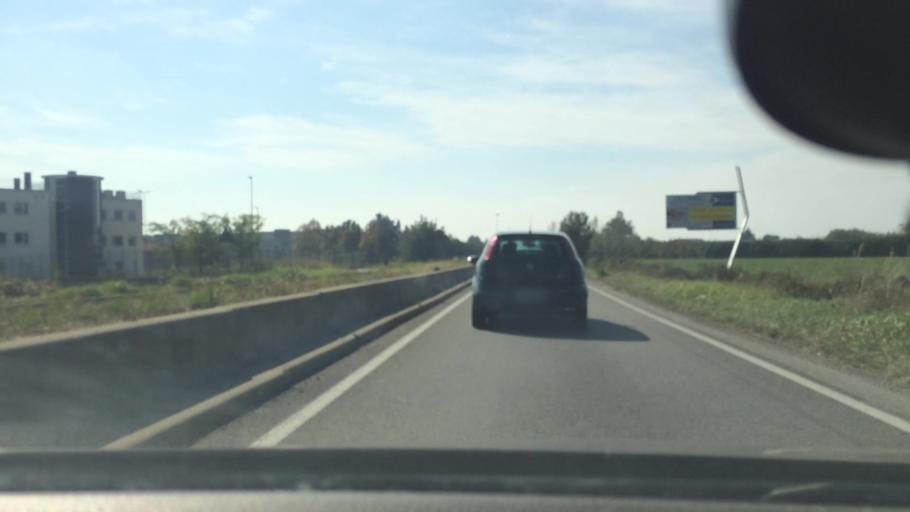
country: IT
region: Lombardy
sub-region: Citta metropolitana di Milano
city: San Giorgio Su Legnano
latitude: 45.5752
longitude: 8.9024
